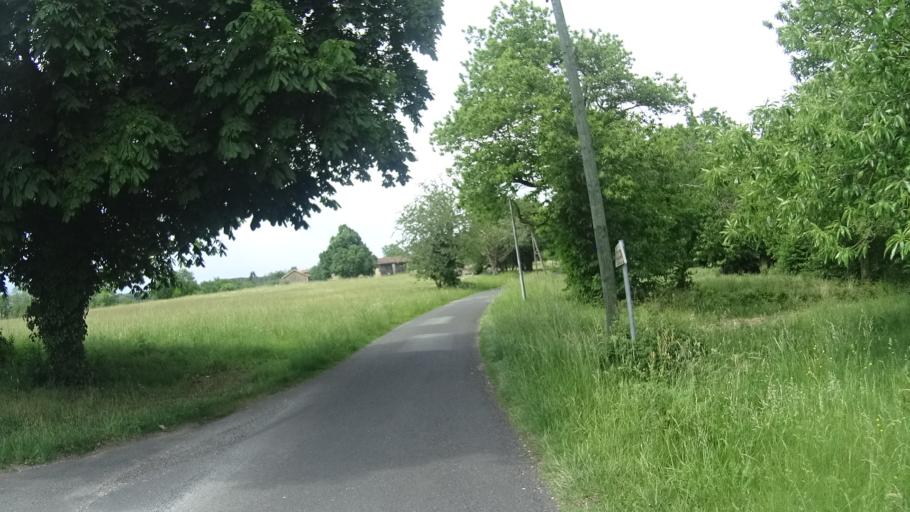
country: FR
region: Aquitaine
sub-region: Departement de la Dordogne
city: Neuvic
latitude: 45.0114
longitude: 0.5459
